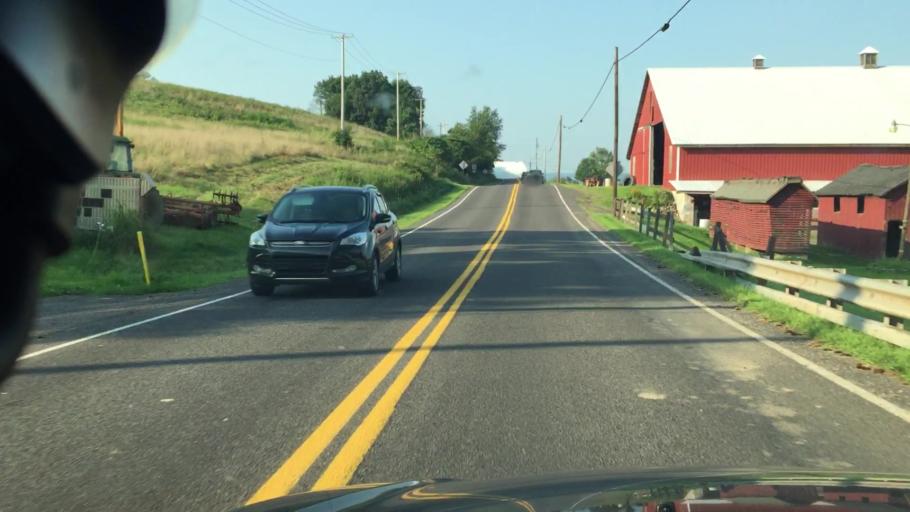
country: US
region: Pennsylvania
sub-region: Columbia County
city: Mifflinville
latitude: 41.0003
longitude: -76.3241
